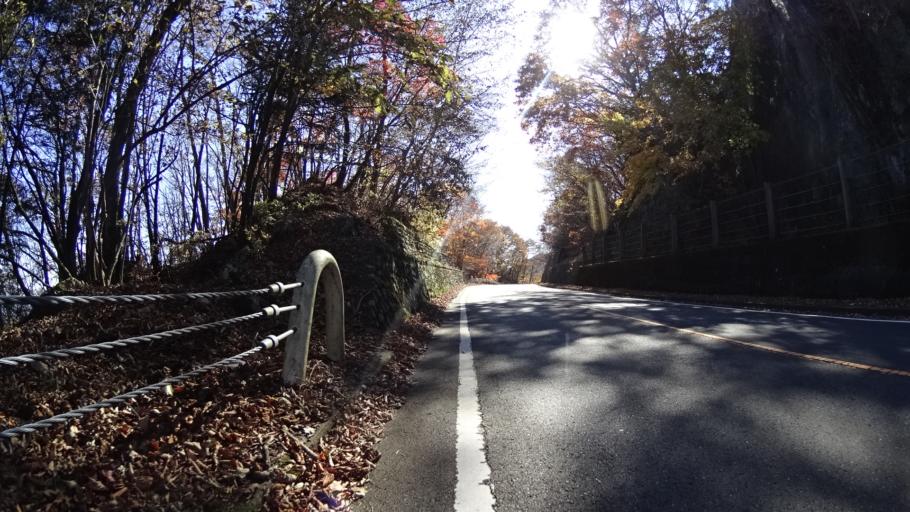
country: JP
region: Yamanashi
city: Uenohara
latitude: 35.7565
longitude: 139.0433
